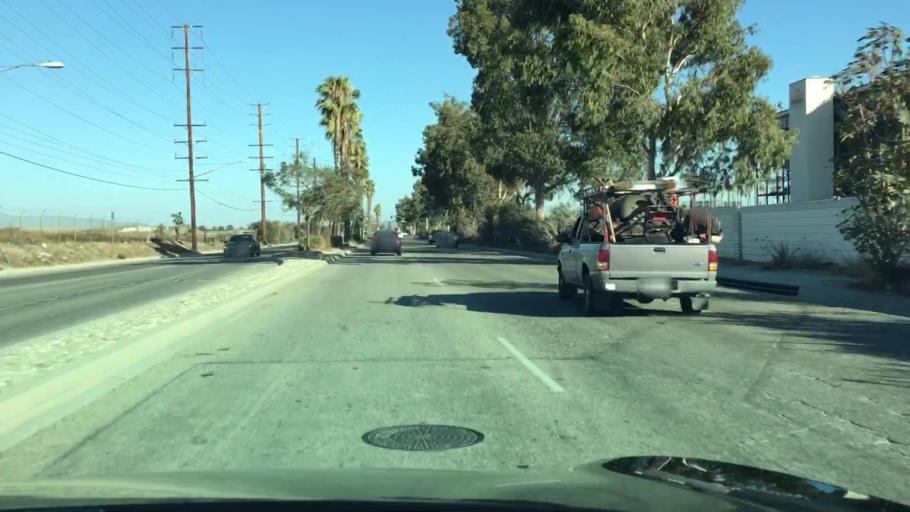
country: US
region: California
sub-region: Los Angeles County
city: Mayflower Village
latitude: 34.1117
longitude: -117.9885
